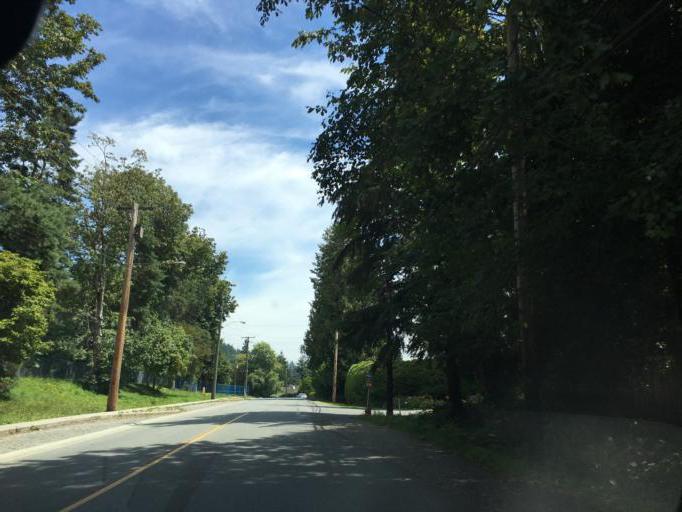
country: CA
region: British Columbia
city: West Vancouver
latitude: 49.3407
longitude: -123.2387
